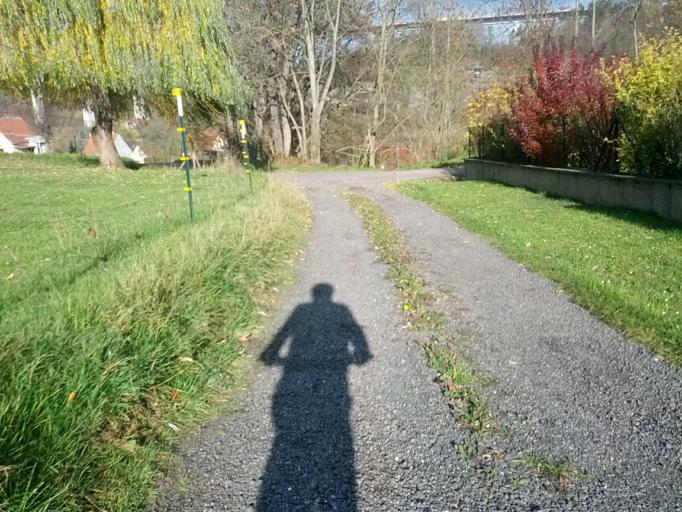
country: DE
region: Thuringia
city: Krauthausen
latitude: 51.0045
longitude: 10.2339
